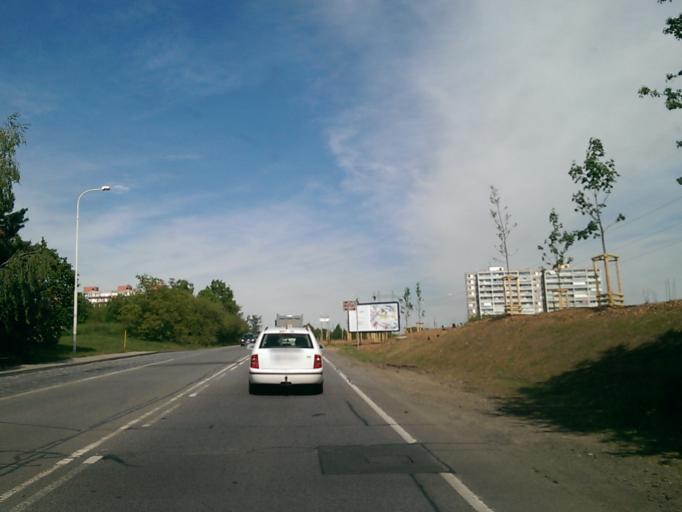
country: CZ
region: Central Bohemia
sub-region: Okres Praha-Zapad
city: Pruhonice
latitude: 50.0332
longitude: 14.5595
